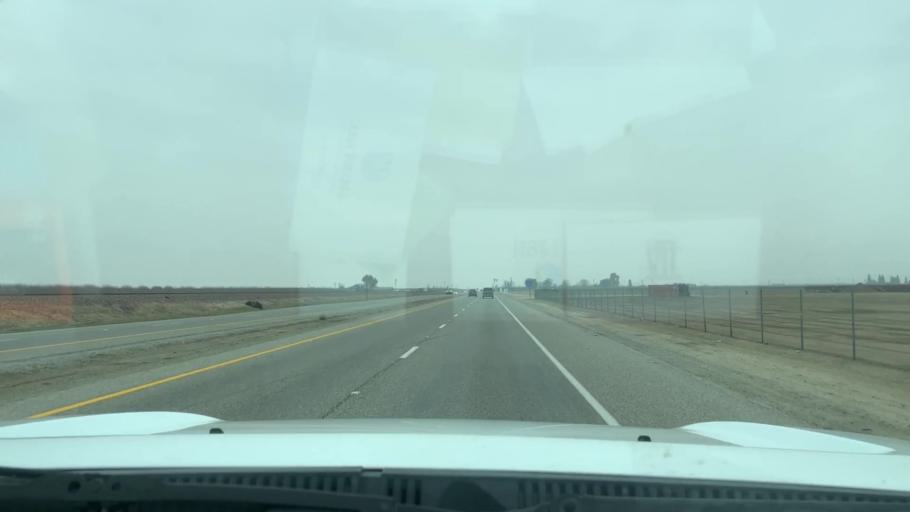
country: US
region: California
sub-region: Kern County
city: Shafter
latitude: 35.5250
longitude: -119.3013
